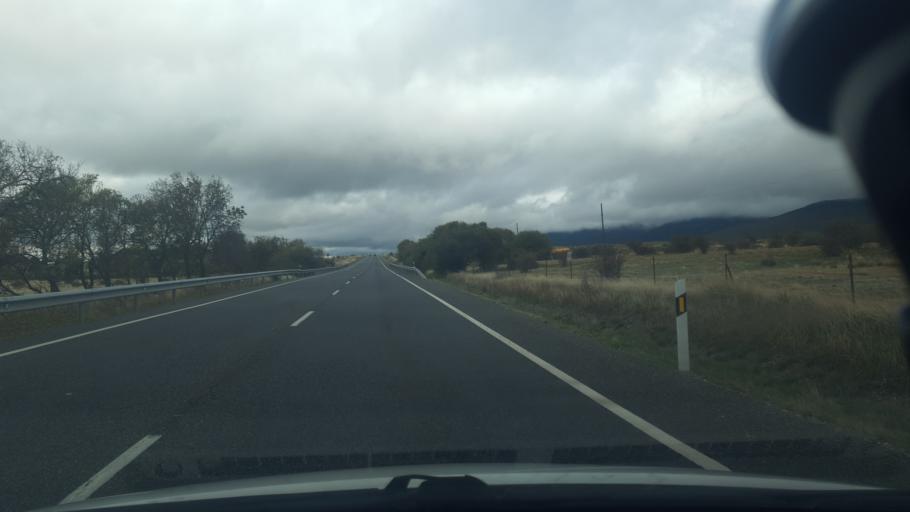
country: ES
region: Castille and Leon
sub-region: Provincia de Segovia
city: Santo Domingo de Piron
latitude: 41.0141
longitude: -3.9762
